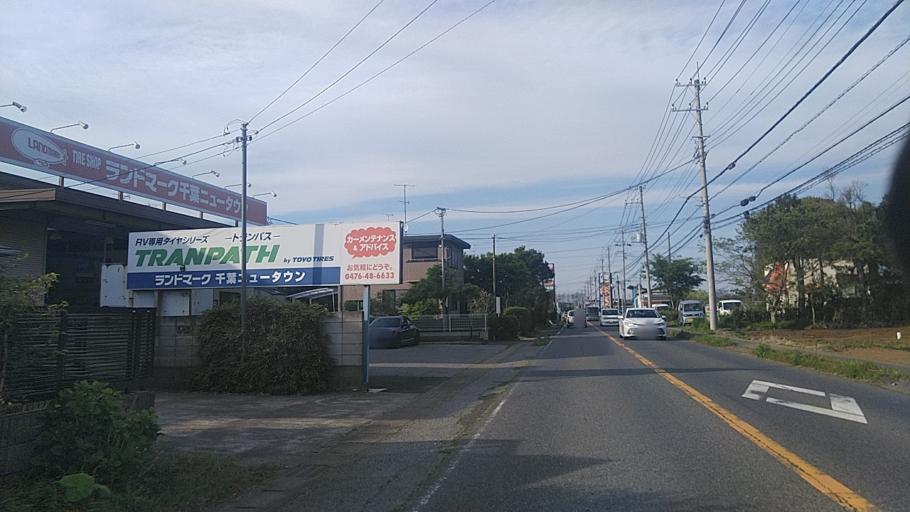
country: JP
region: Chiba
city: Shiroi
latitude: 35.7897
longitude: 140.1312
